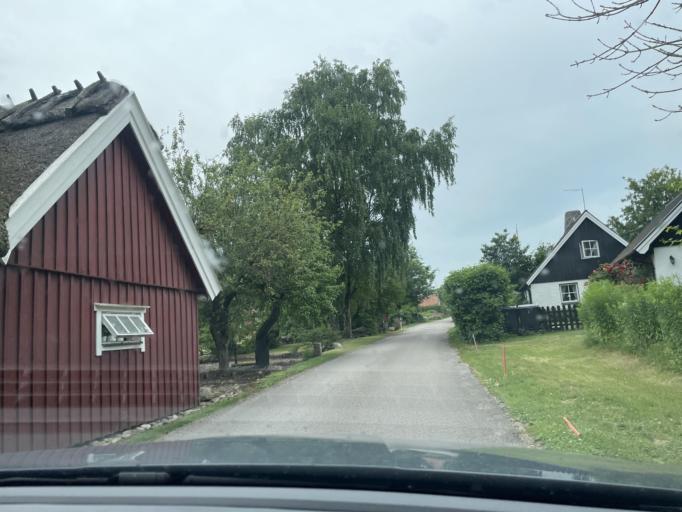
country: SE
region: Skane
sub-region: Bromolla Kommun
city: Bromoella
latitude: 56.0084
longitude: 14.4353
